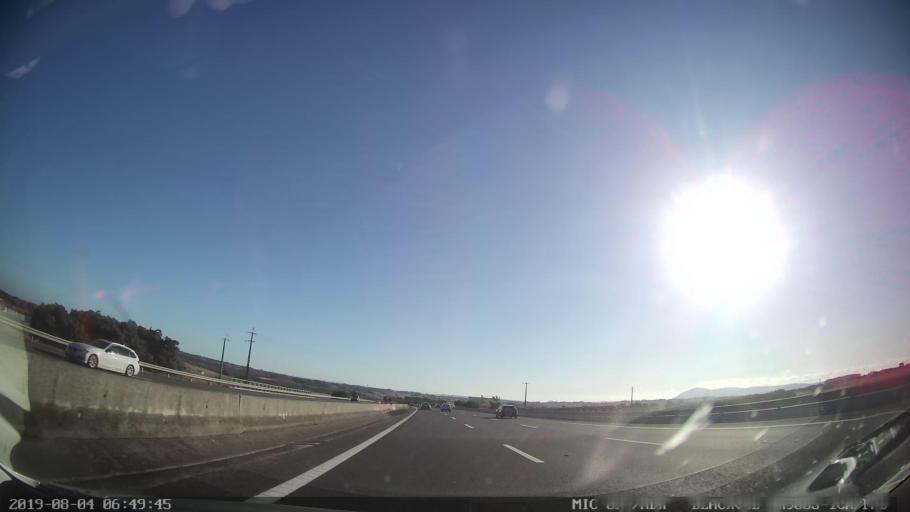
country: PT
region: Santarem
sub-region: Cartaxo
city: Pontevel
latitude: 39.1714
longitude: -8.8439
